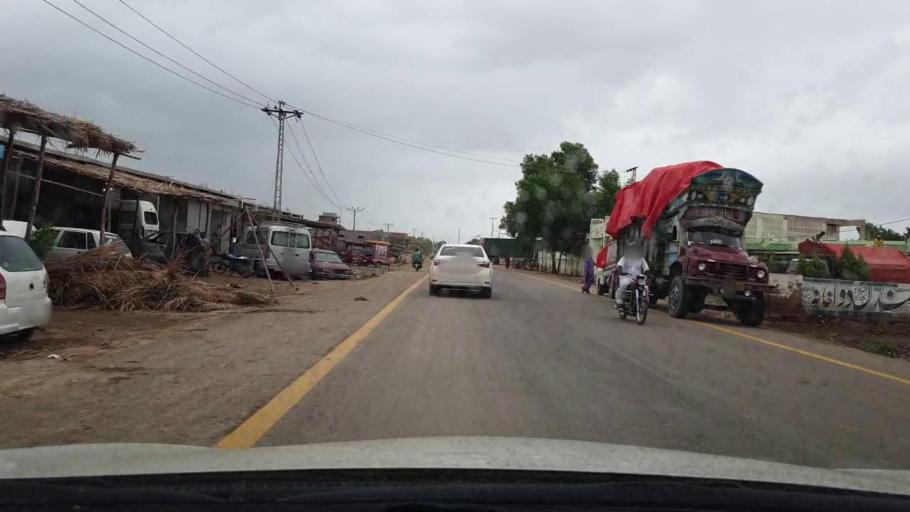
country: PK
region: Sindh
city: Badin
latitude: 24.6555
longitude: 68.8200
